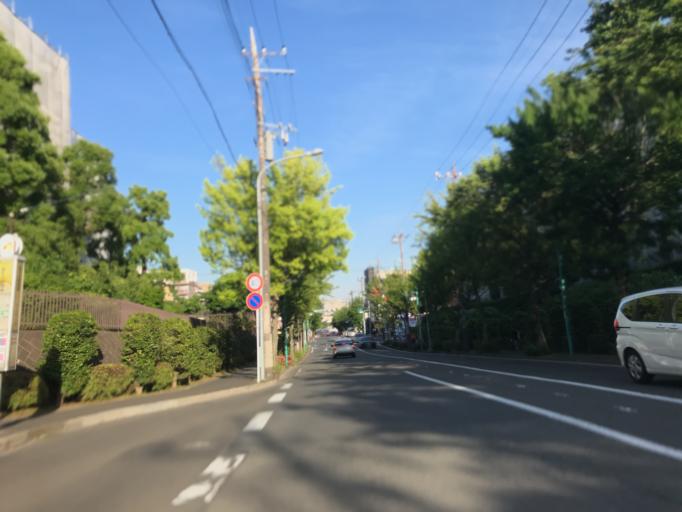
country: JP
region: Tokyo
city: Chofugaoka
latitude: 35.5703
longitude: 139.5429
